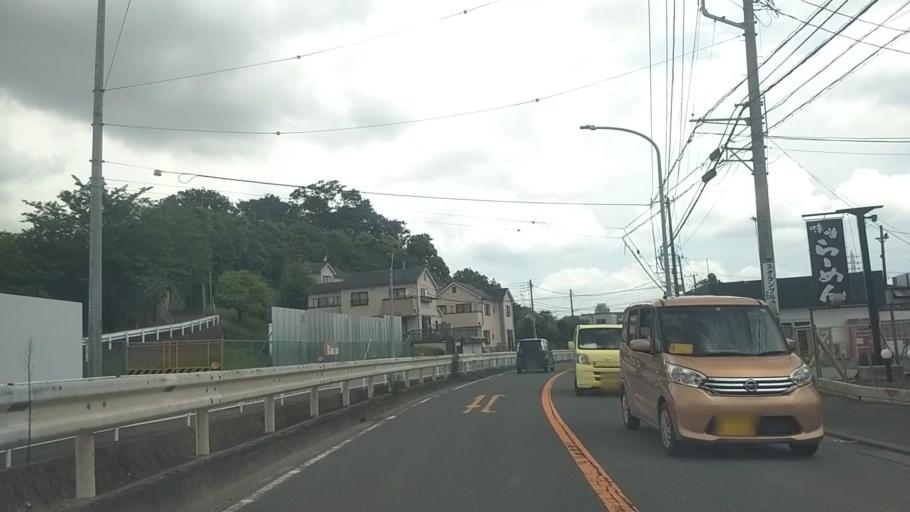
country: JP
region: Kanagawa
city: Fujisawa
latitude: 35.3704
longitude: 139.5218
